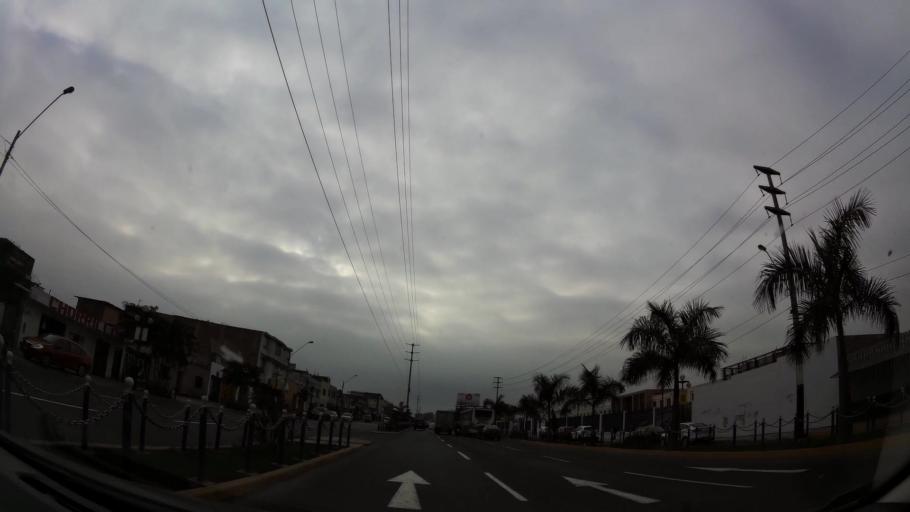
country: PE
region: Lima
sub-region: Lima
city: Surco
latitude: -12.1933
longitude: -77.0033
